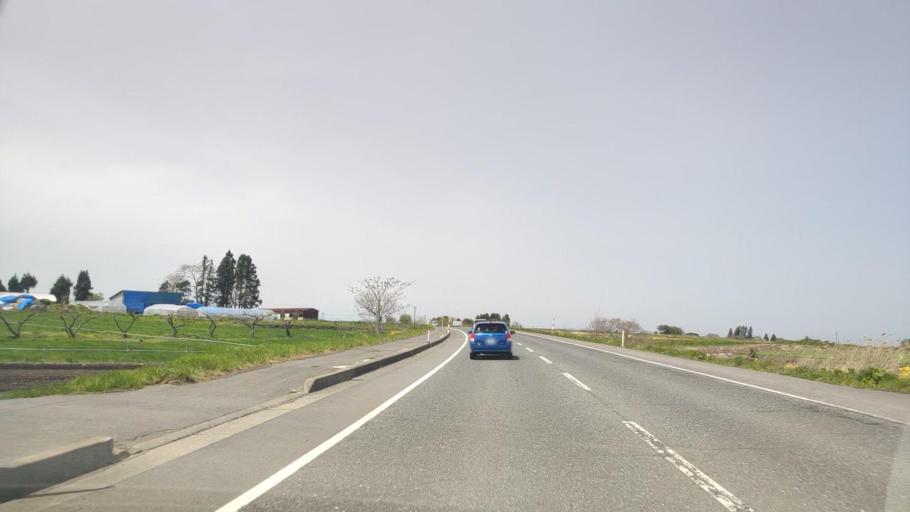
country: JP
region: Aomori
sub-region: Misawa Shi
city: Inuotose
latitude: 40.6363
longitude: 141.2426
